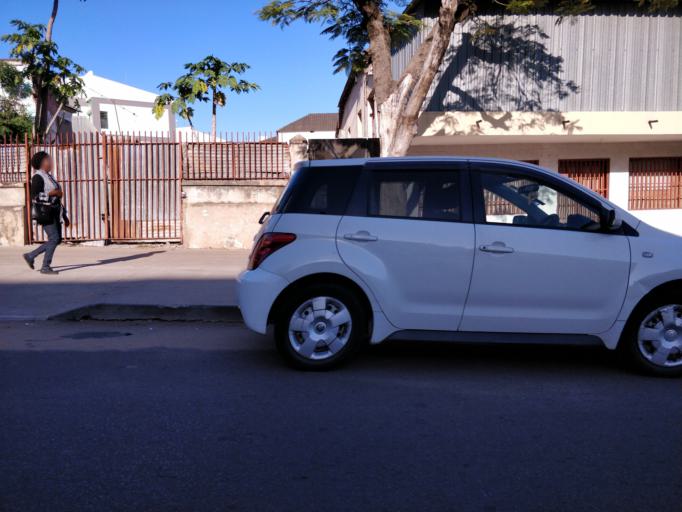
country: MZ
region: Maputo City
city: Maputo
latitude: -25.9661
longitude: 32.5668
